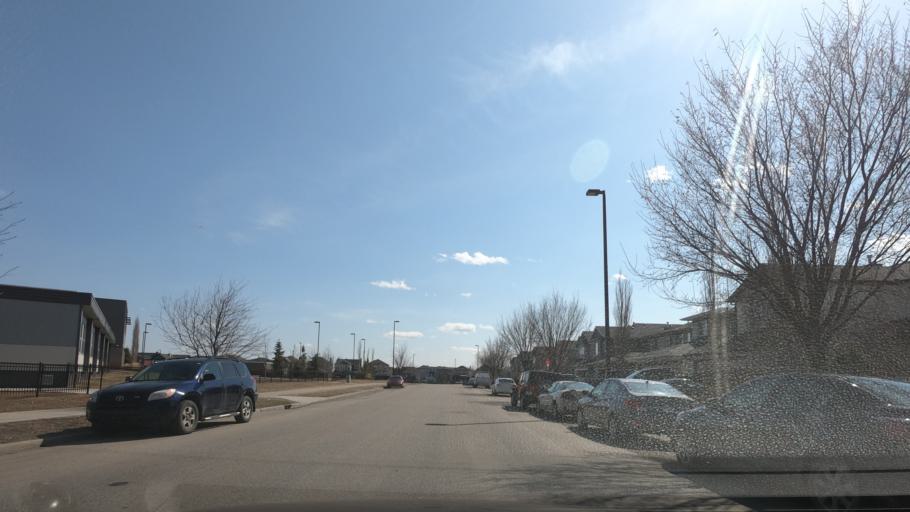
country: CA
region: Alberta
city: Airdrie
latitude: 51.2903
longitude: -114.0425
